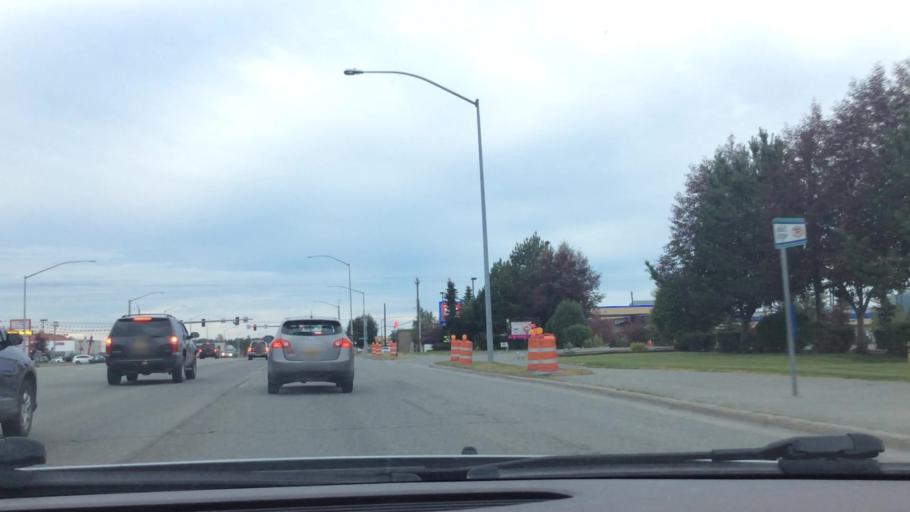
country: US
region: Alaska
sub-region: Anchorage Municipality
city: Anchorage
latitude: 61.1808
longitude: -149.8647
